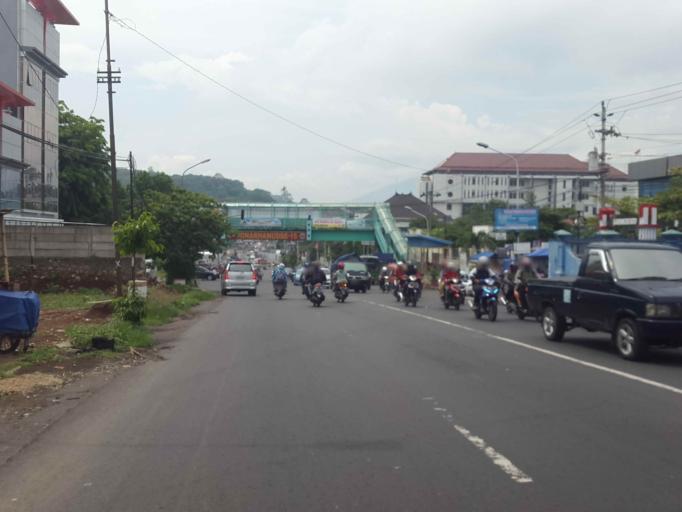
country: ID
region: Central Java
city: Semarang
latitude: -7.0284
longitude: 110.4184
